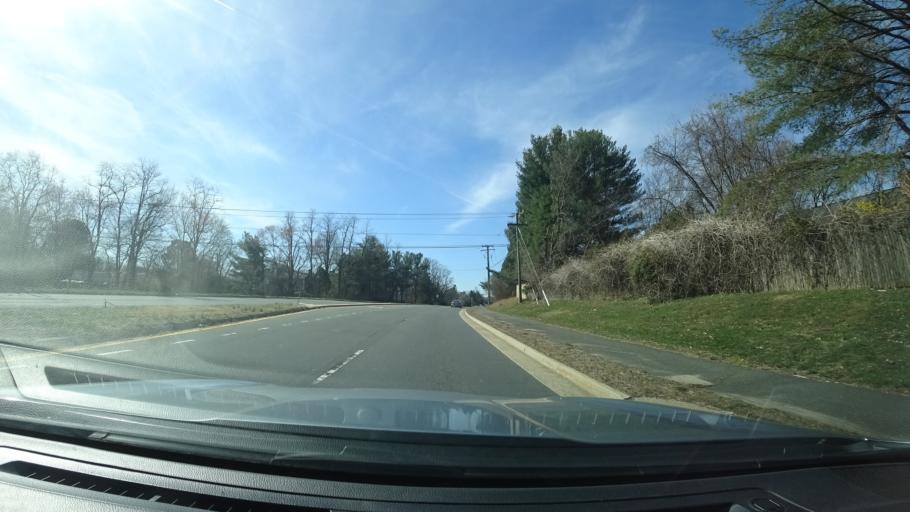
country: US
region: Virginia
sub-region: Fairfax County
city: Oak Hill
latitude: 38.9243
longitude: -77.3738
